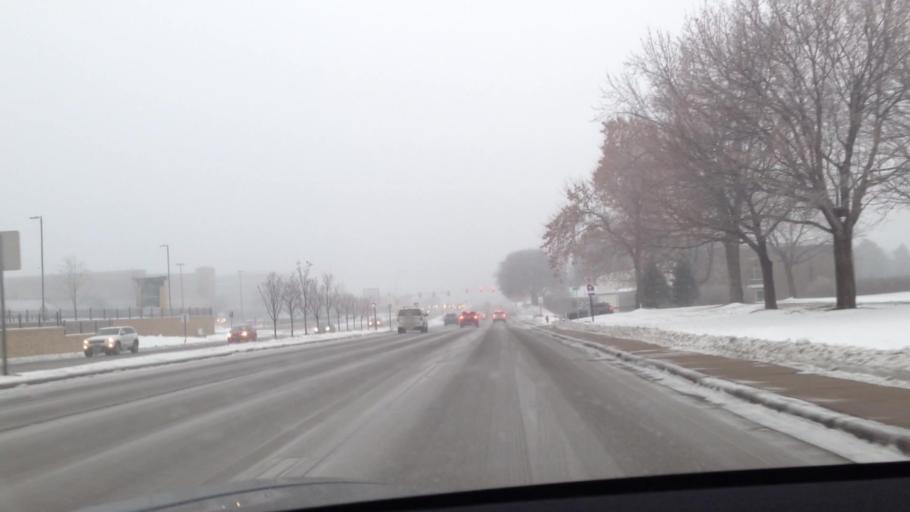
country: US
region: Minnesota
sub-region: Hennepin County
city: Edina
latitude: 44.8736
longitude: -93.3291
